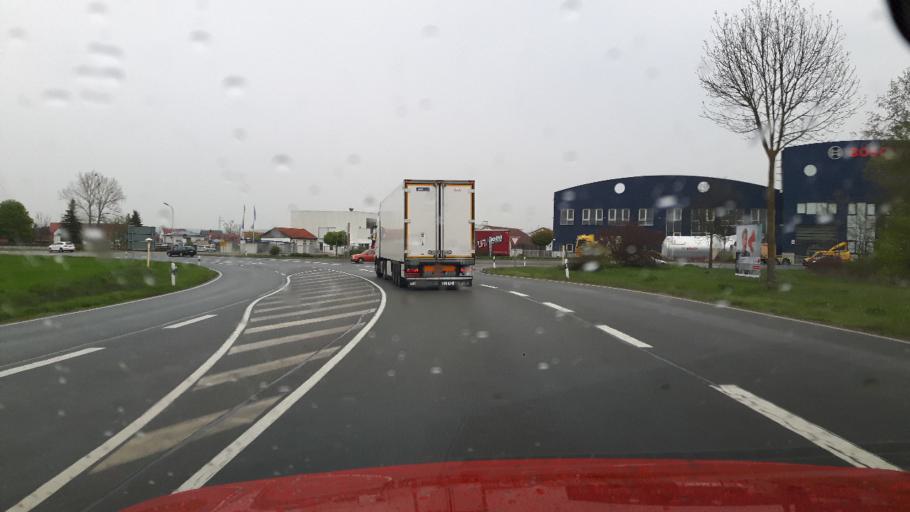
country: DE
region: Bavaria
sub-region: Regierungsbezirk Mittelfranken
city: Gunzenhausen
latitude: 49.1246
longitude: 10.7502
